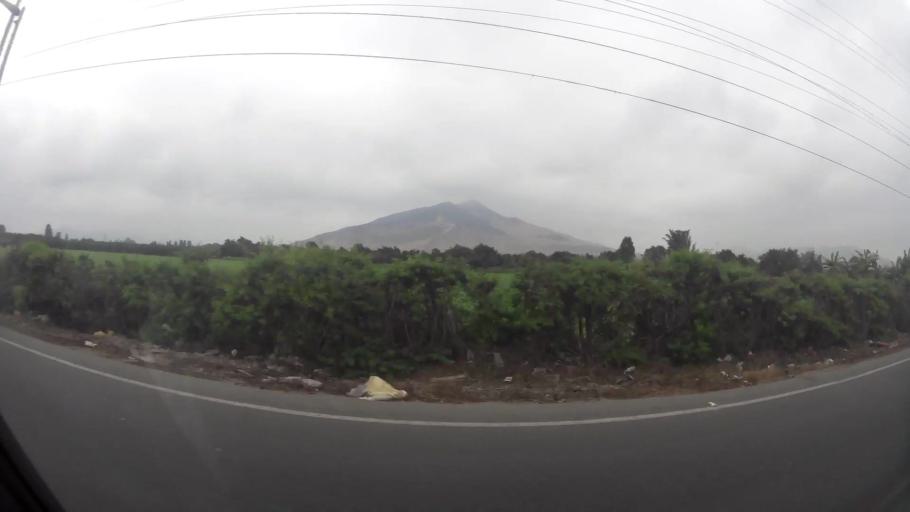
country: PE
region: Lima
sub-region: Provincia de Huaral
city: Huaral
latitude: -11.5136
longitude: -77.2345
